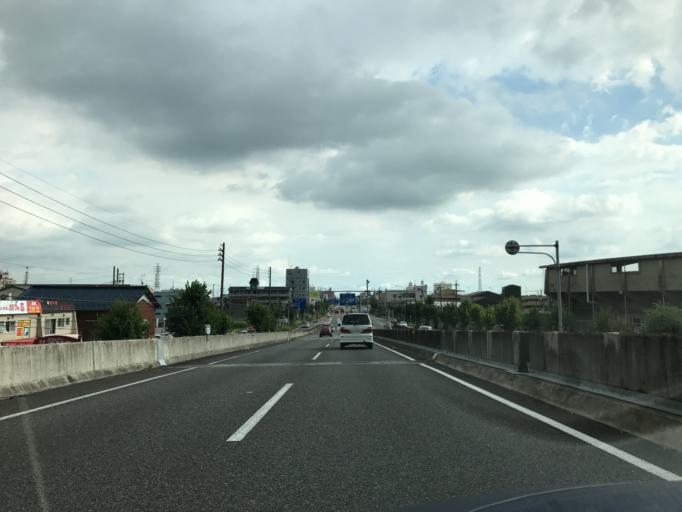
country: JP
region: Gifu
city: Gifu-shi
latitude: 35.4142
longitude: 136.7852
